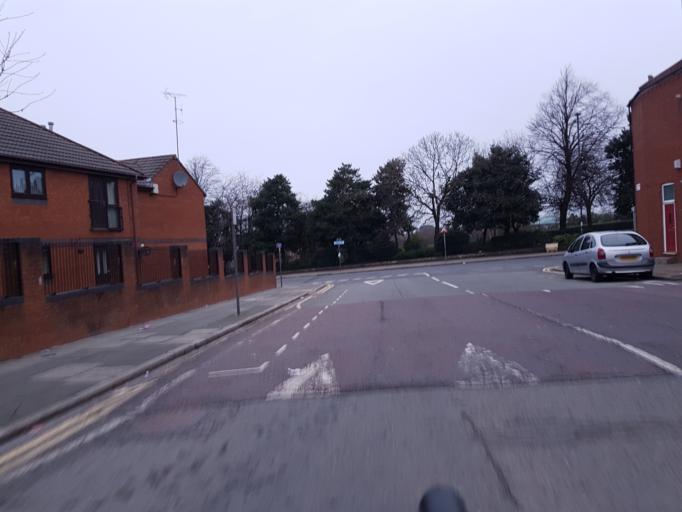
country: GB
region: England
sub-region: Liverpool
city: Liverpool
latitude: 53.4327
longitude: -2.9680
